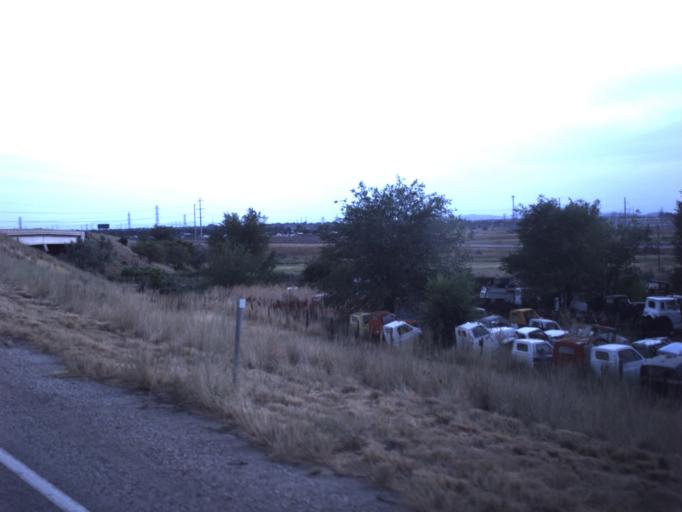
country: US
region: Utah
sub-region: Box Elder County
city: South Willard
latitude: 41.3455
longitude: -112.0334
